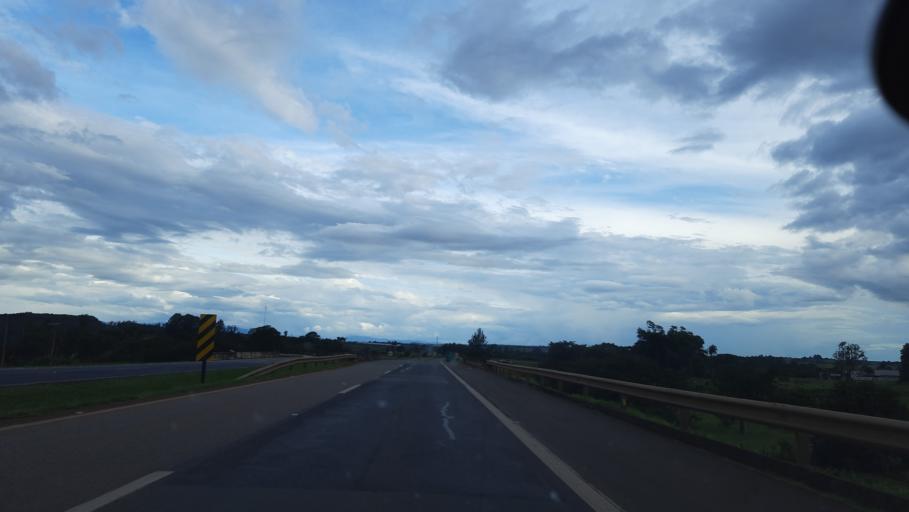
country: BR
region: Sao Paulo
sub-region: Casa Branca
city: Casa Branca
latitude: -21.7711
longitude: -47.0648
